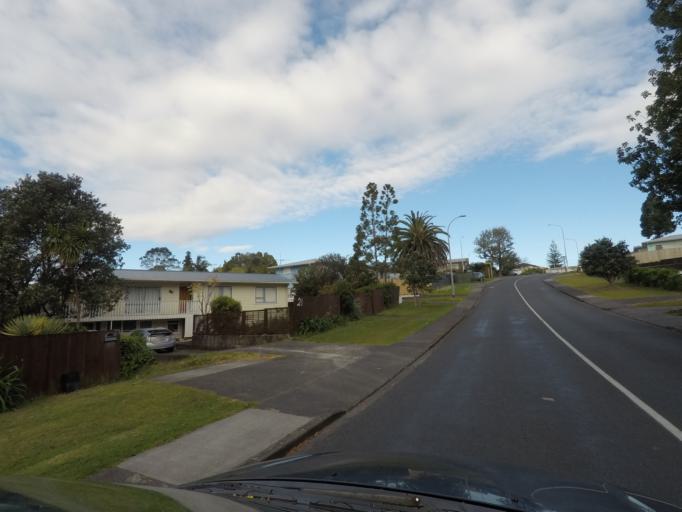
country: NZ
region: Auckland
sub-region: Auckland
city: Rosebank
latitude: -36.8890
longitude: 174.6526
